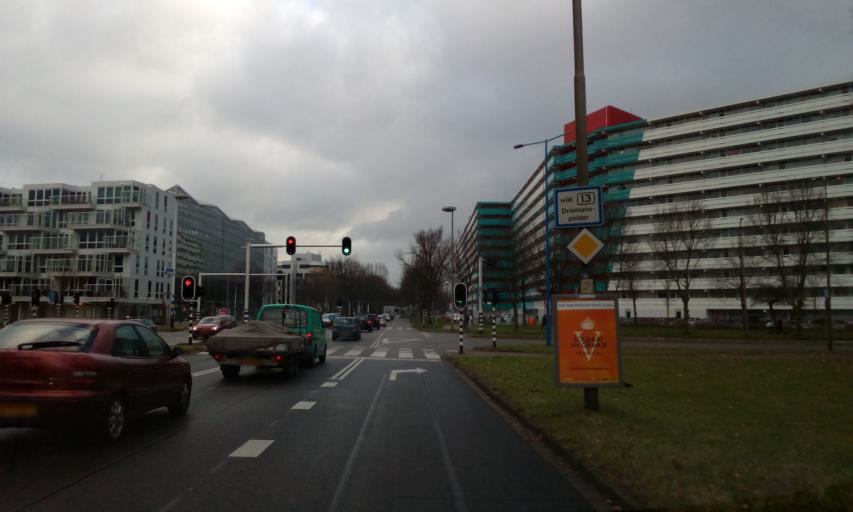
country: NL
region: South Holland
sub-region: Gemeente Zoetermeer
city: Zoetermeer
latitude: 52.0576
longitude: 4.4816
